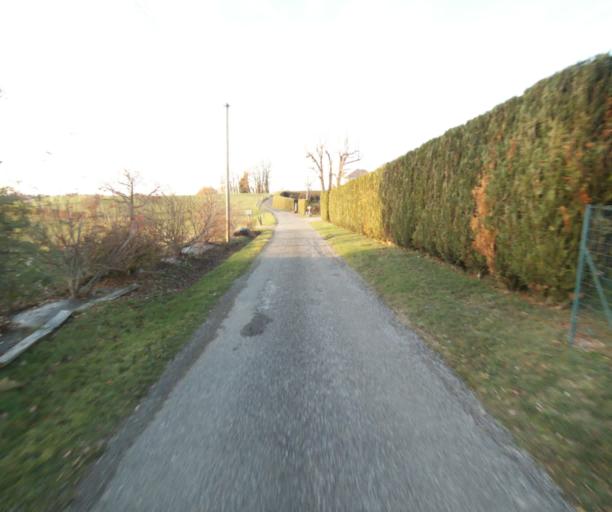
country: FR
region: Limousin
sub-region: Departement de la Correze
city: Laguenne
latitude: 45.2297
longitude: 1.8238
